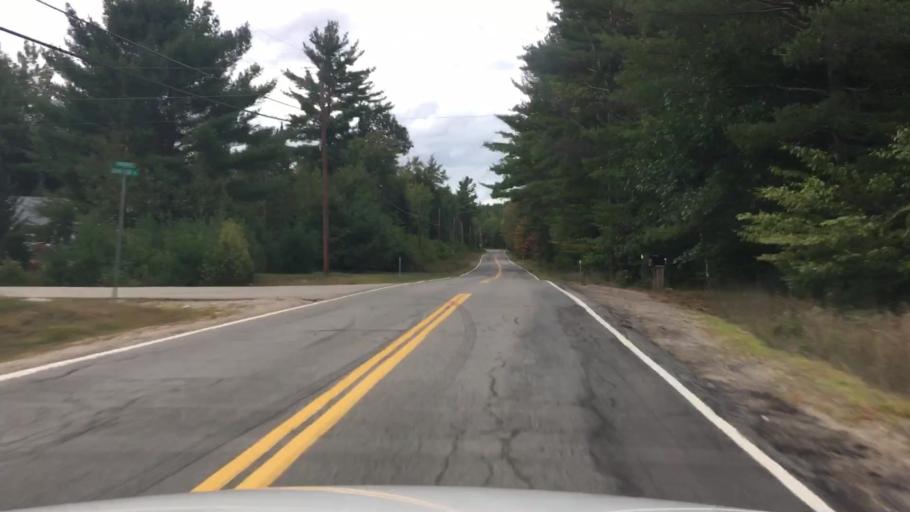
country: US
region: New Hampshire
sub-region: Carroll County
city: Effingham
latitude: 43.7464
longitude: -71.0040
